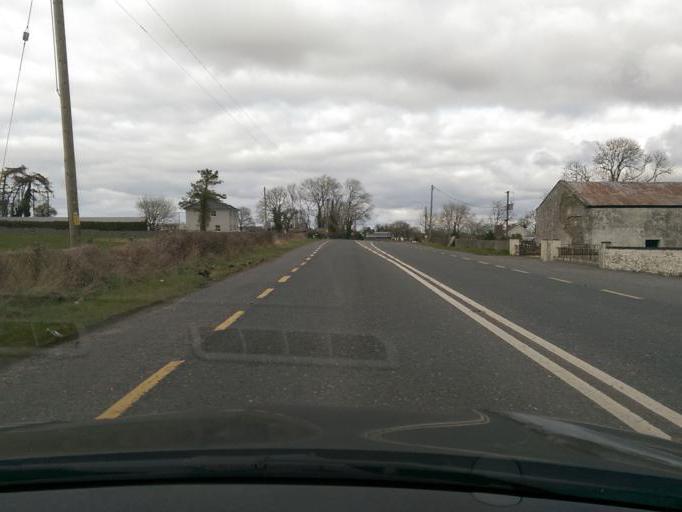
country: IE
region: Leinster
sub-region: An Iarmhi
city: Athlone
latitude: 53.3900
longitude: -7.9920
